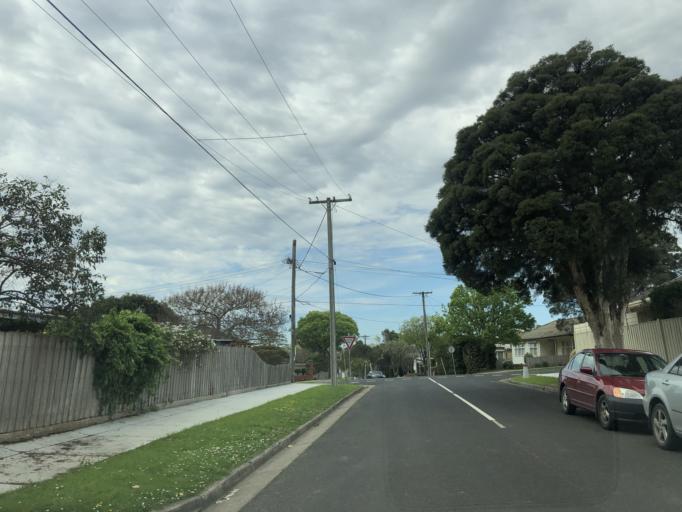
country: AU
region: Victoria
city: Burwood East
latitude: -37.8502
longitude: 145.1387
